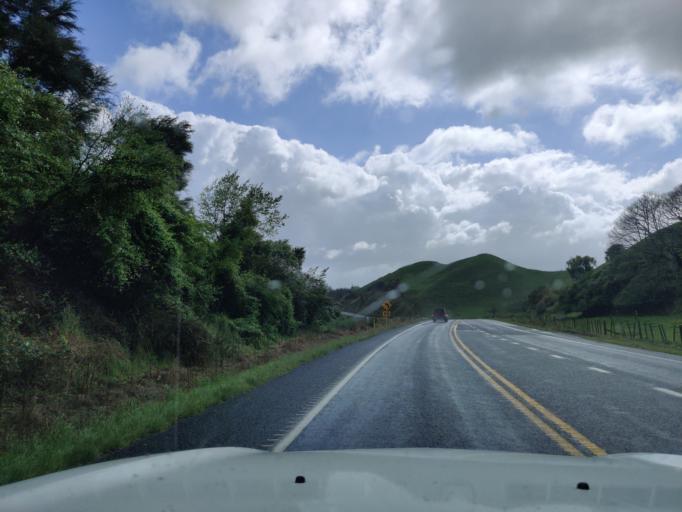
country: NZ
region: Waikato
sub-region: Matamata-Piako District
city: Matamata
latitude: -37.9781
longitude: 175.7399
